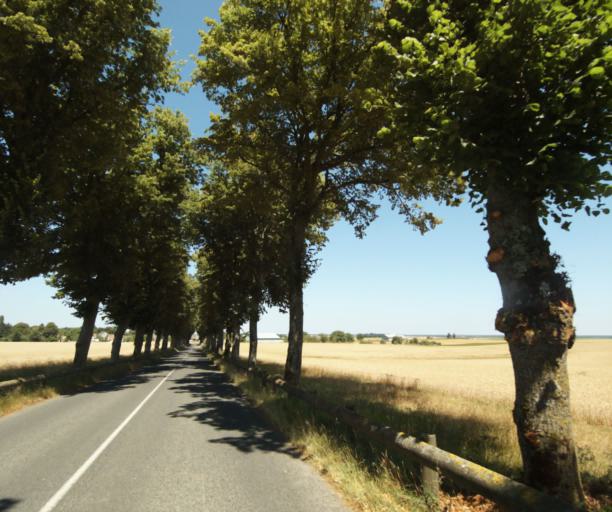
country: FR
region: Ile-de-France
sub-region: Departement de Seine-et-Marne
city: Noisy-sur-Ecole
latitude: 48.3417
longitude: 2.4577
